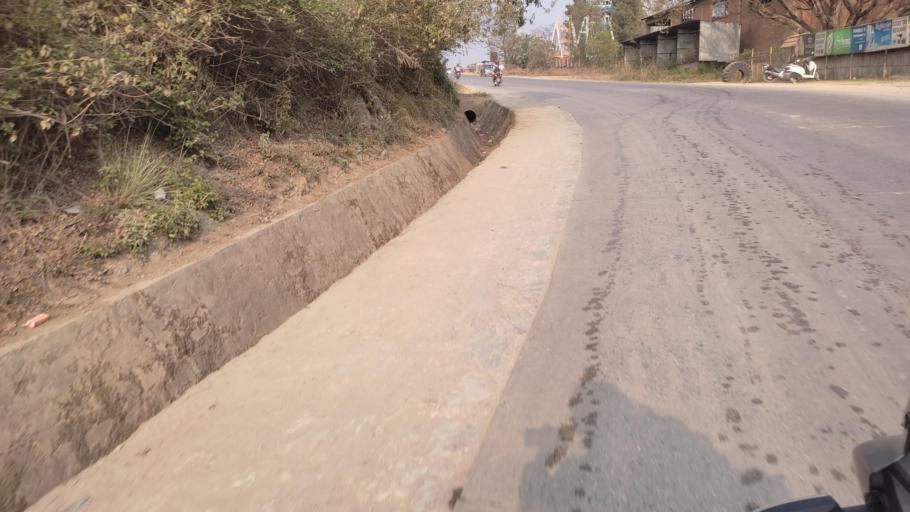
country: NP
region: Central Region
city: Kirtipur
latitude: 27.6606
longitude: 85.2919
